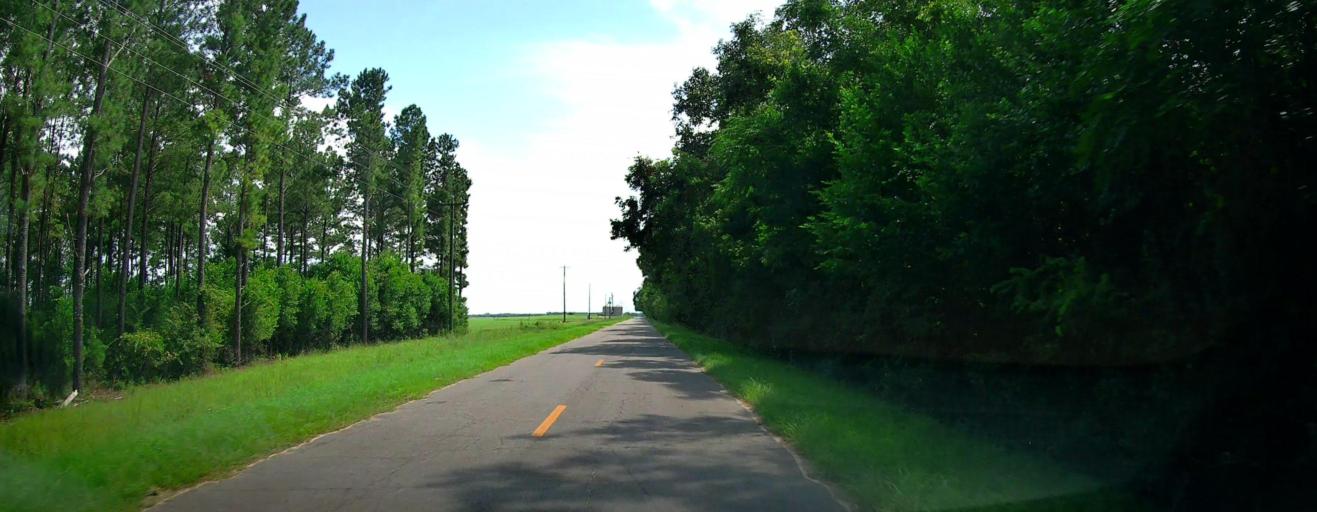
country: US
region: Georgia
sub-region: Macon County
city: Marshallville
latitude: 32.4441
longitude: -84.0006
